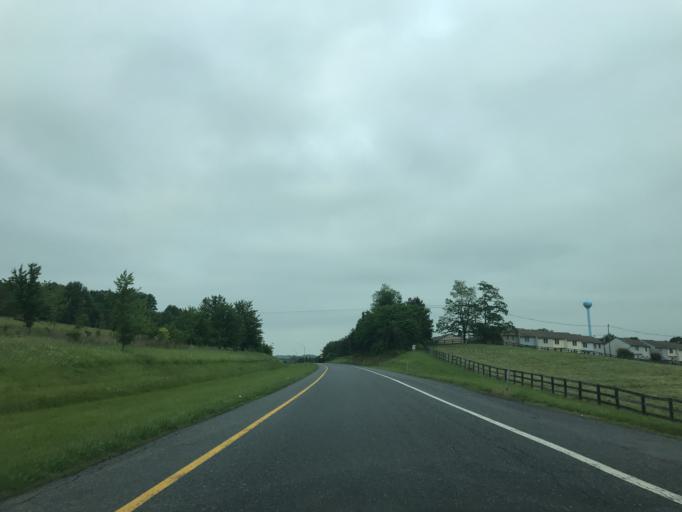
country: US
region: Maryland
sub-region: Frederick County
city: Thurmont
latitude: 39.6350
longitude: -77.4091
